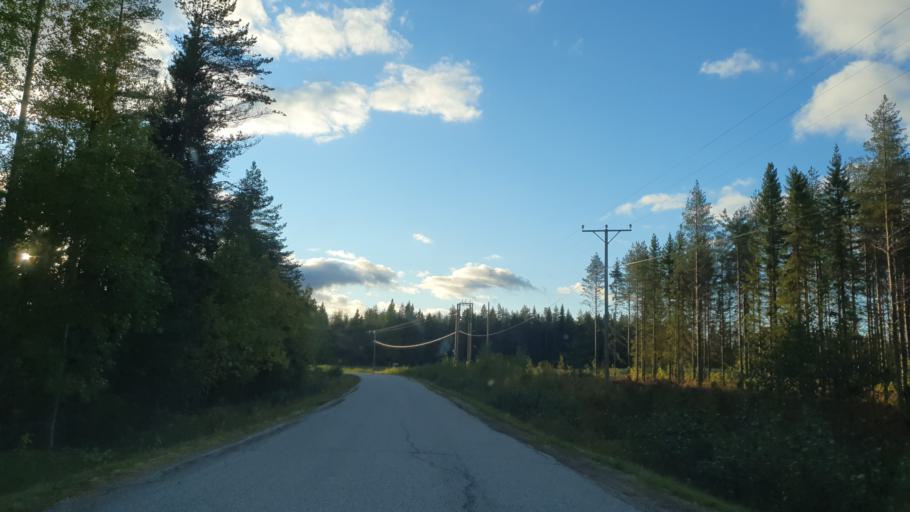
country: FI
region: Kainuu
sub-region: Kehys-Kainuu
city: Kuhmo
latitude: 63.9548
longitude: 29.7337
